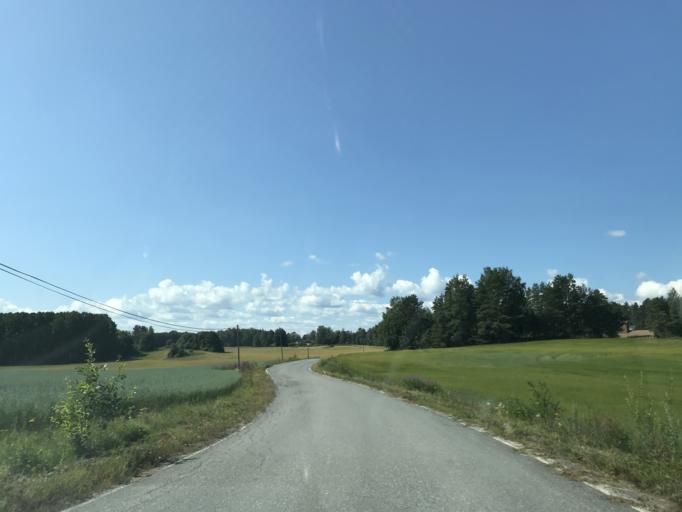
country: FI
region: Paijanne Tavastia
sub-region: Lahti
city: Asikkala
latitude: 61.1954
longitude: 25.6234
